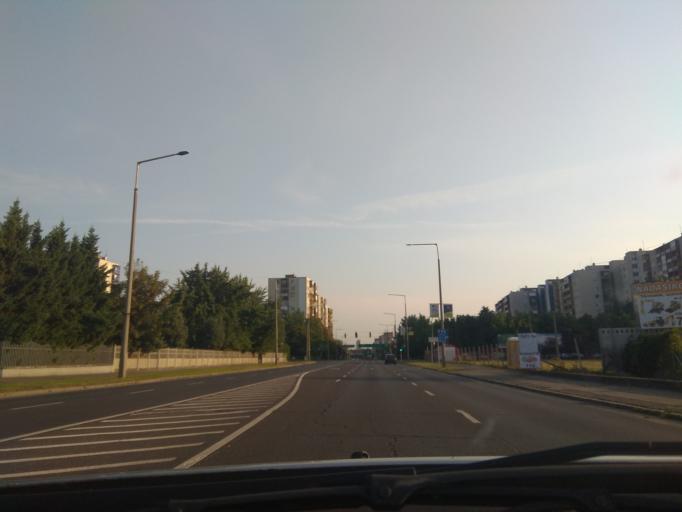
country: HU
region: Borsod-Abauj-Zemplen
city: Miskolc
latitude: 48.0965
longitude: 20.7926
